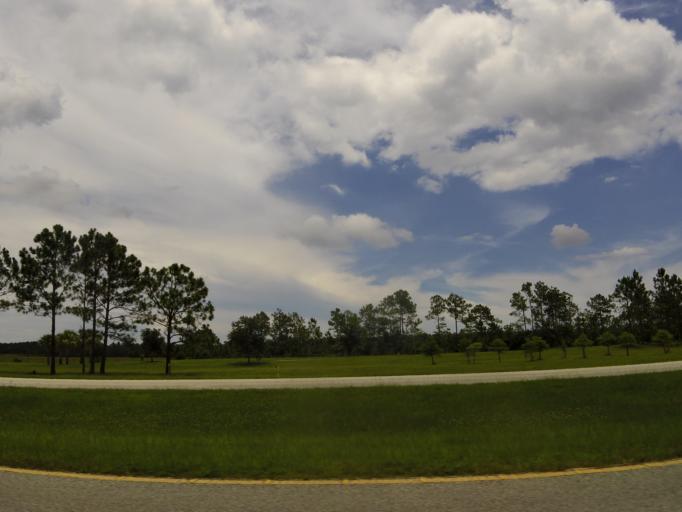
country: US
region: Florida
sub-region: Flagler County
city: Palm Coast
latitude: 29.5748
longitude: -81.2758
